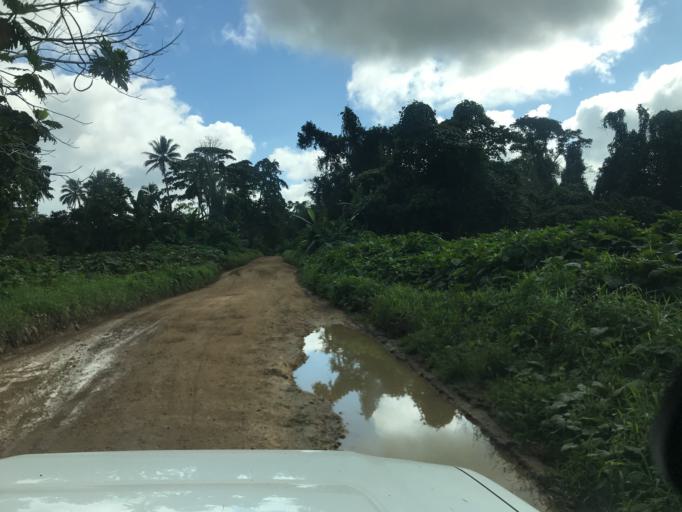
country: VU
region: Sanma
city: Luganville
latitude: -15.4933
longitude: 167.0895
